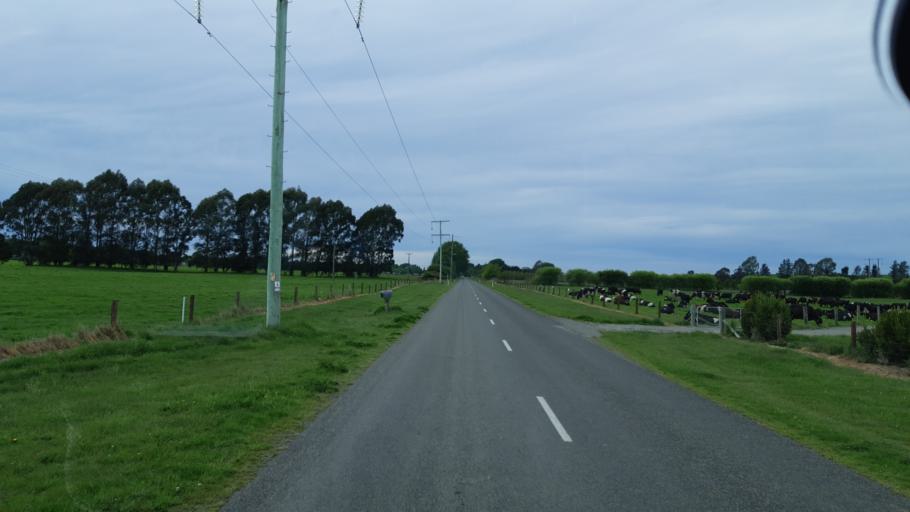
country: NZ
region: Canterbury
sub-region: Timaru District
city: Timaru
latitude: -44.4786
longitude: 171.1448
